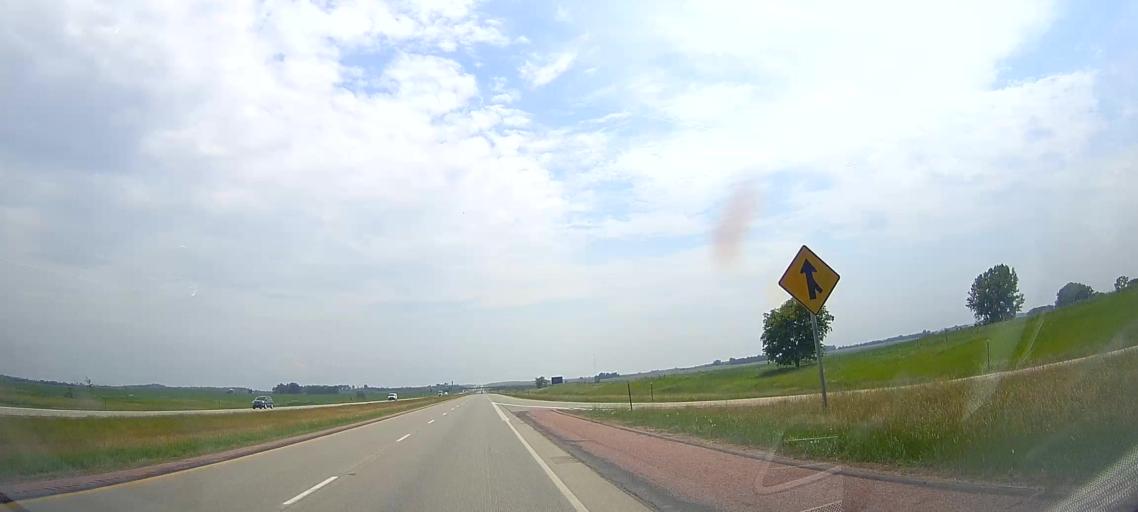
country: US
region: South Dakota
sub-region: Union County
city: Beresford
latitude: 42.9505
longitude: -96.7951
